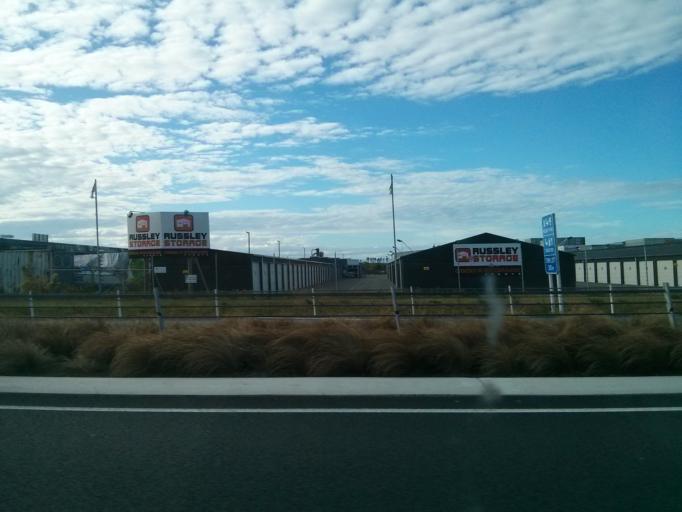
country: NZ
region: Canterbury
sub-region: Christchurch City
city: Christchurch
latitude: -43.4726
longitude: 172.5660
